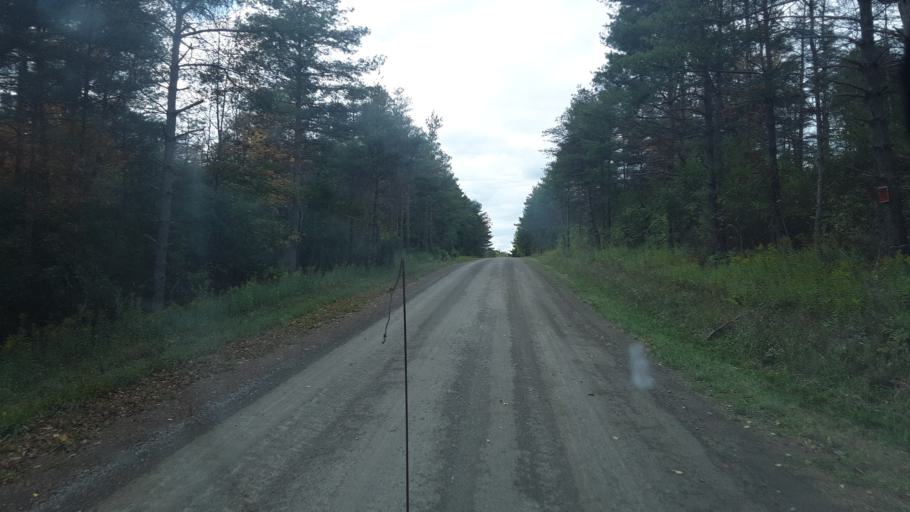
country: US
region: New York
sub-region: Allegany County
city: Alfred
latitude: 42.3909
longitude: -77.8736
